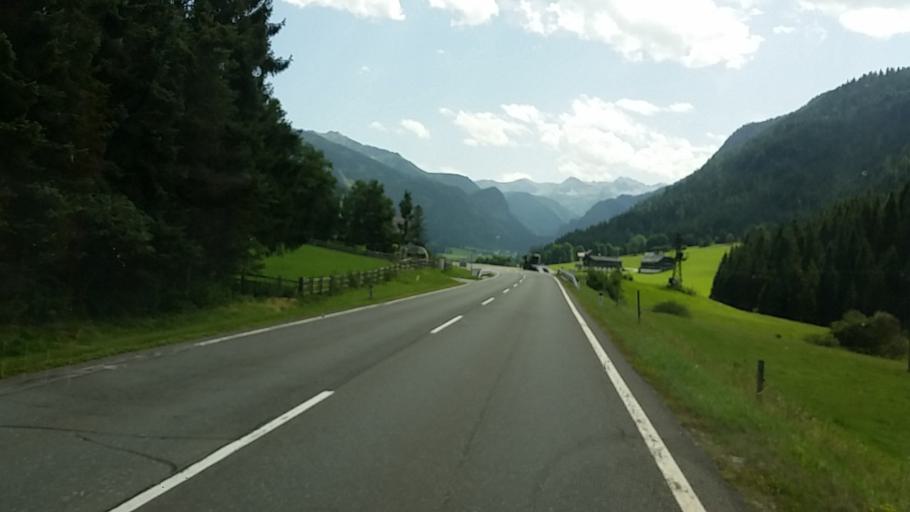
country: AT
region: Salzburg
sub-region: Politischer Bezirk Sankt Johann im Pongau
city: Untertauern
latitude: 47.3383
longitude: 13.5044
